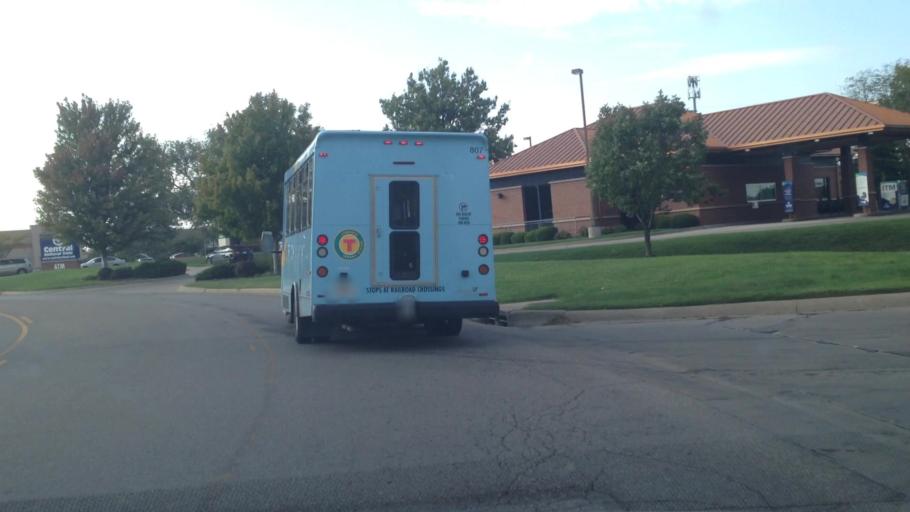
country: US
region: Kansas
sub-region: Douglas County
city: Lawrence
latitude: 38.9266
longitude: -95.2616
